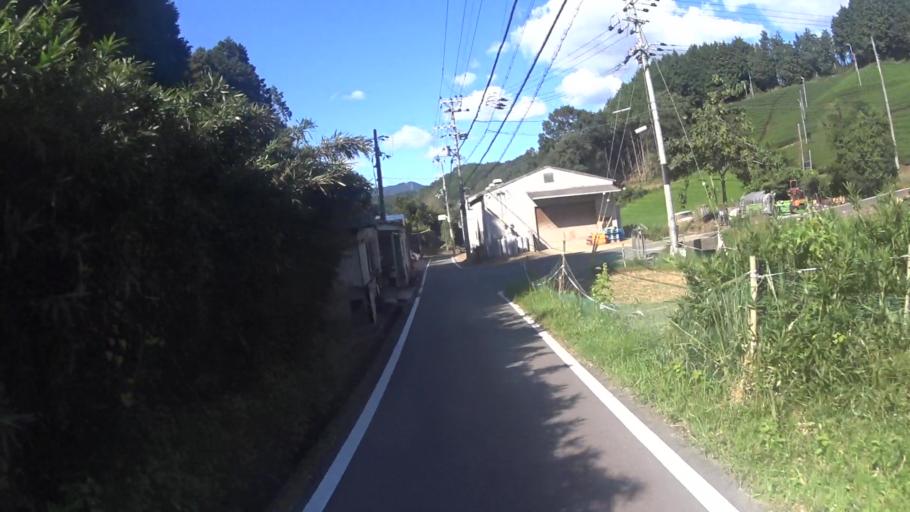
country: JP
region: Nara
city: Nara-shi
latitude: 34.7802
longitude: 135.9079
